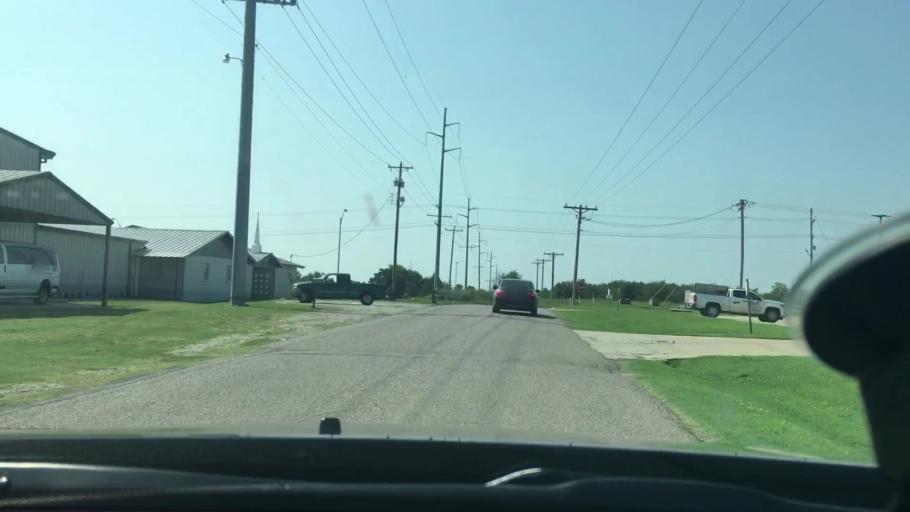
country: US
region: Oklahoma
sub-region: Bryan County
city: Durant
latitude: 33.9988
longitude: -96.4253
